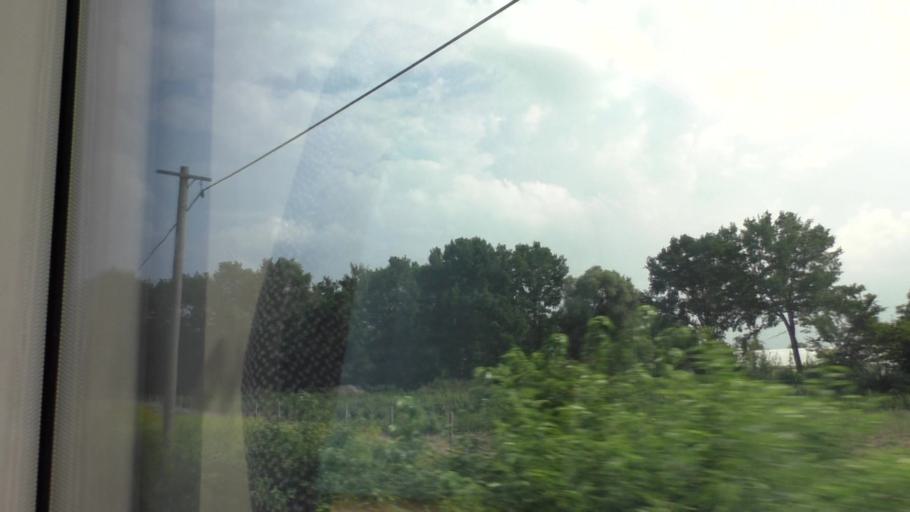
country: DE
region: Brandenburg
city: Erkner
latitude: 52.2939
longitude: 13.7707
